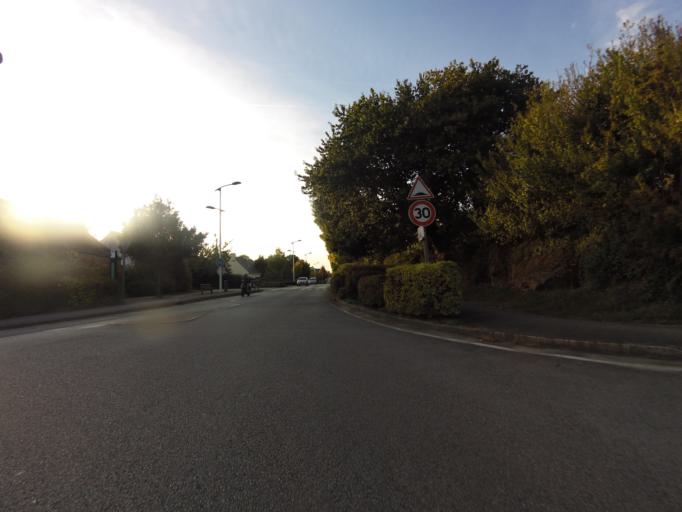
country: FR
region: Brittany
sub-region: Departement du Morbihan
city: Theix
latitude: 47.6282
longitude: -2.6441
